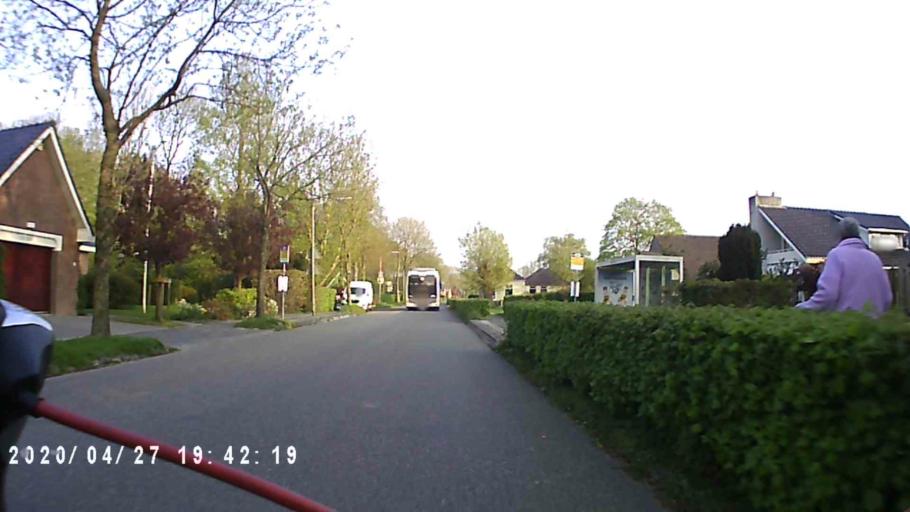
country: NL
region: Groningen
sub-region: Gemeente Winsum
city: Winsum
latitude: 53.3594
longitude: 6.4631
